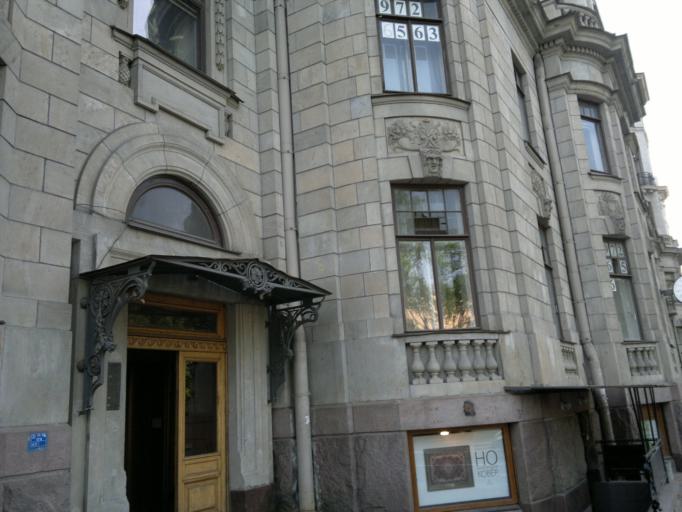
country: RU
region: St.-Petersburg
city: Petrogradka
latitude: 59.9620
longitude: 30.3151
